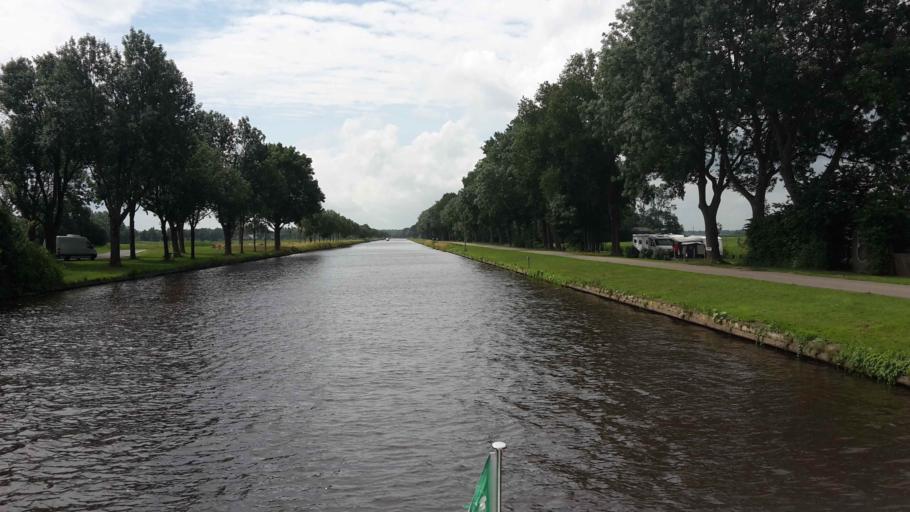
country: NL
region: Overijssel
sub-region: Gemeente Steenwijkerland
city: Tuk
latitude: 52.7718
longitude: 6.0859
